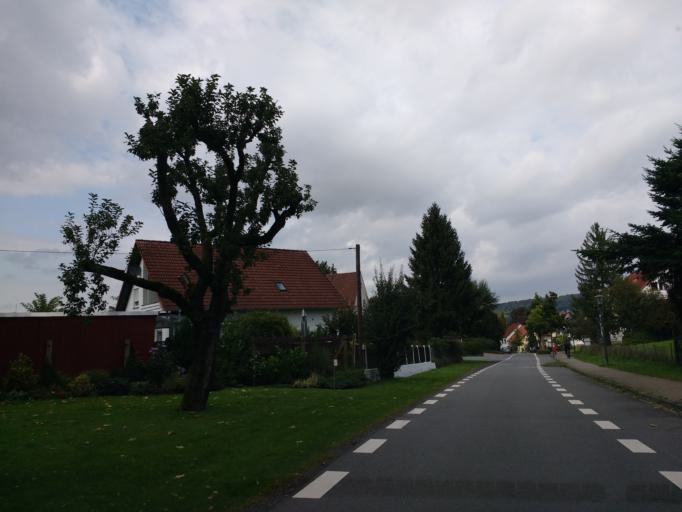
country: DE
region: North Rhine-Westphalia
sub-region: Regierungsbezirk Detmold
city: Lemgo
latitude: 52.0203
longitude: 8.8983
